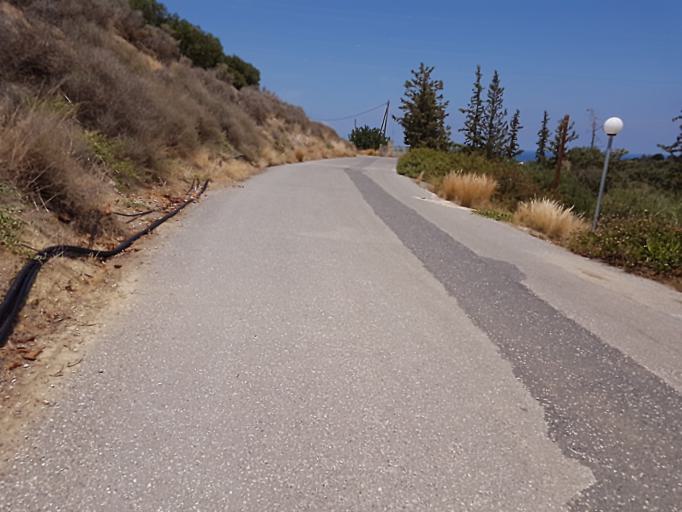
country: GR
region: Crete
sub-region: Nomos Irakleiou
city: Limin Khersonisou
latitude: 35.3114
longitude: 25.3842
